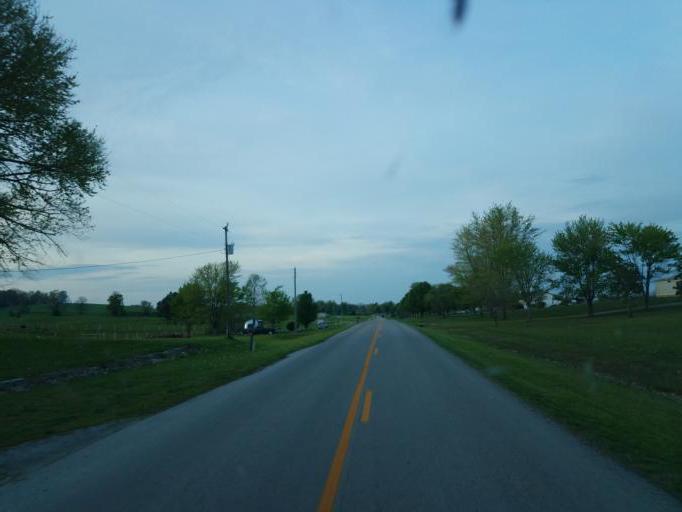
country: US
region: Kentucky
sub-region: Hart County
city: Munfordville
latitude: 37.2233
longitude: -85.7012
